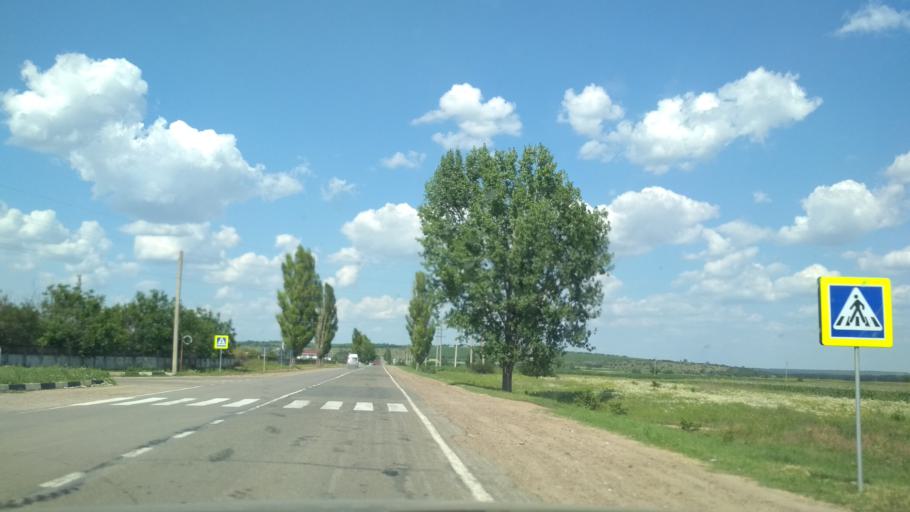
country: MD
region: Criuleni
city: Criuleni
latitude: 47.1457
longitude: 29.1450
